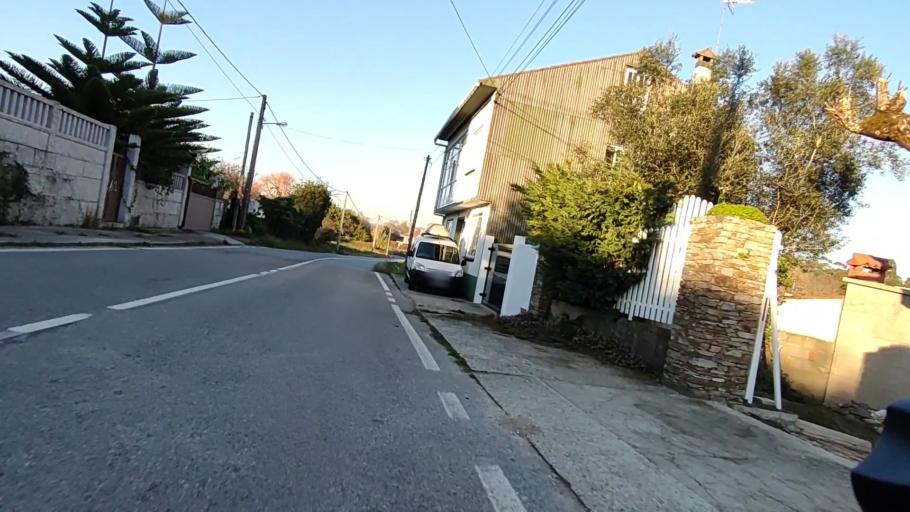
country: ES
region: Galicia
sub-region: Provincia da Coruna
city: Boiro
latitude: 42.6297
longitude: -8.8607
